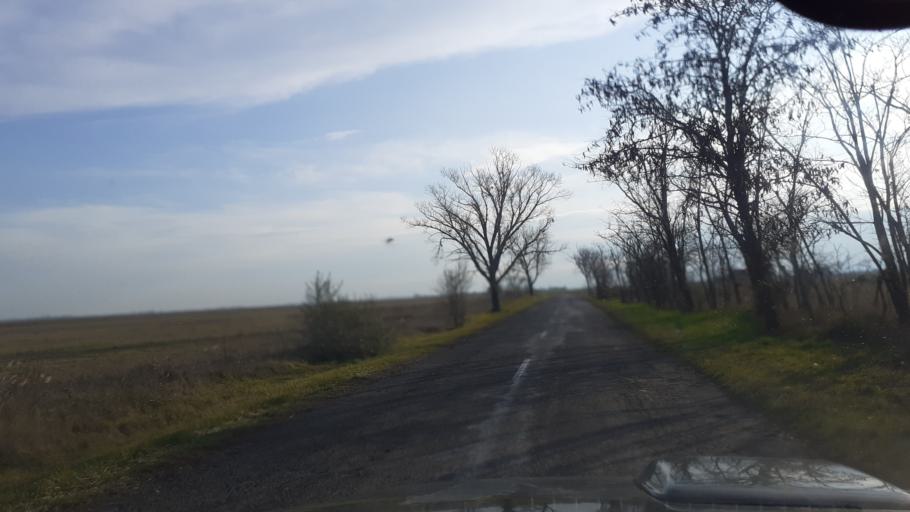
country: HU
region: Bacs-Kiskun
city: Kunszentmiklos
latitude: 47.0902
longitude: 19.0942
